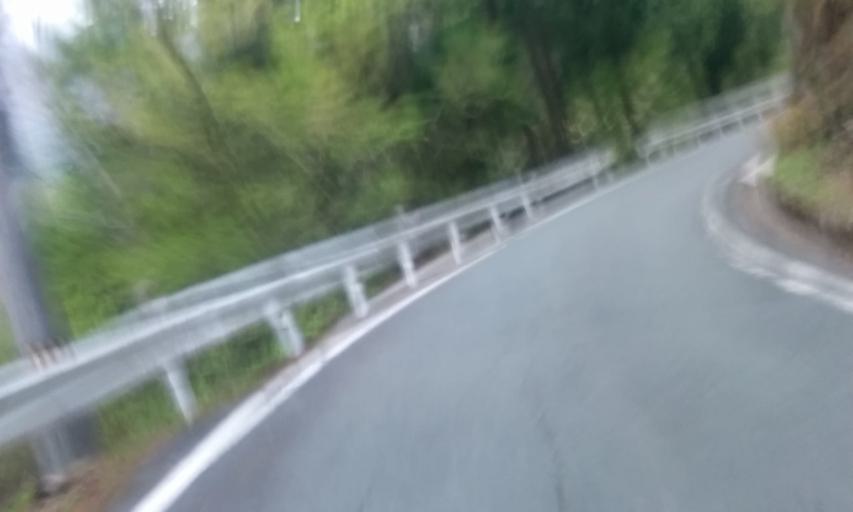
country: JP
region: Ehime
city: Saijo
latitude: 33.8028
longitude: 133.2735
